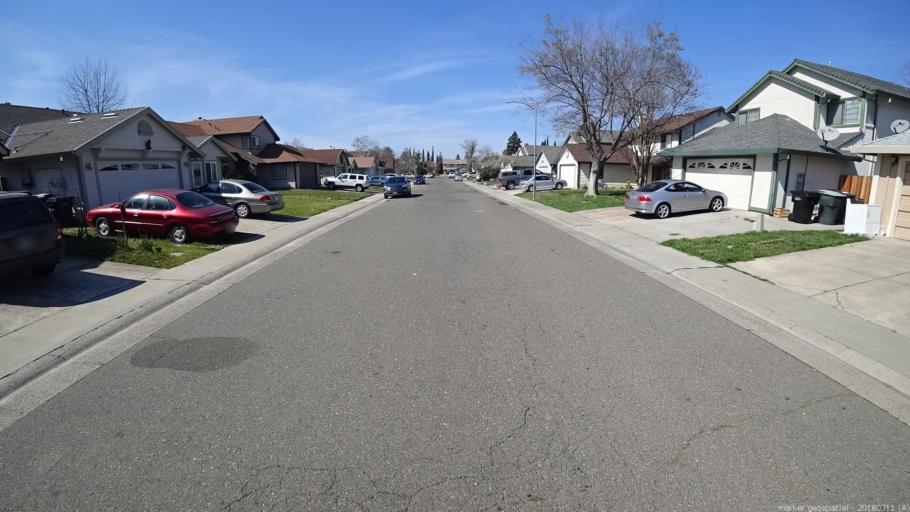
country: US
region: California
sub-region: Sacramento County
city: Florin
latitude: 38.4612
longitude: -121.3960
